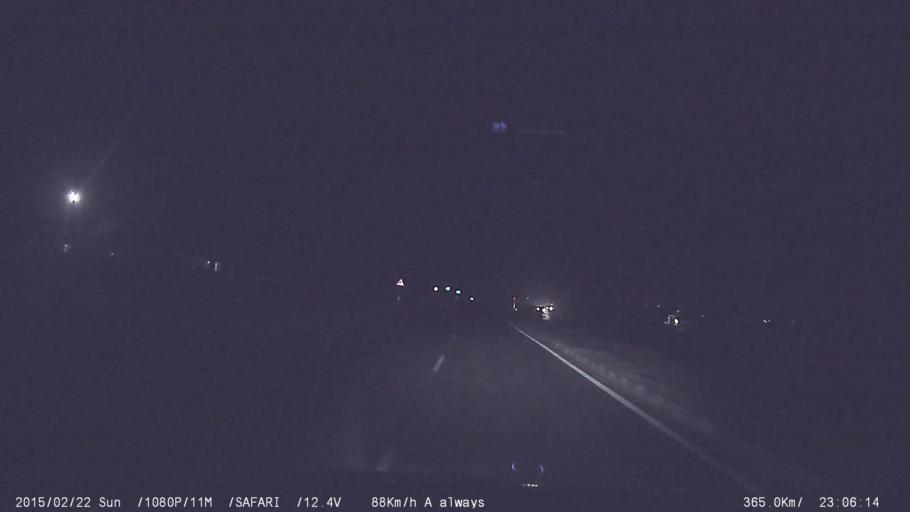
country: IN
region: Tamil Nadu
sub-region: Namakkal
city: Rasipuram
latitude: 11.4251
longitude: 78.1560
